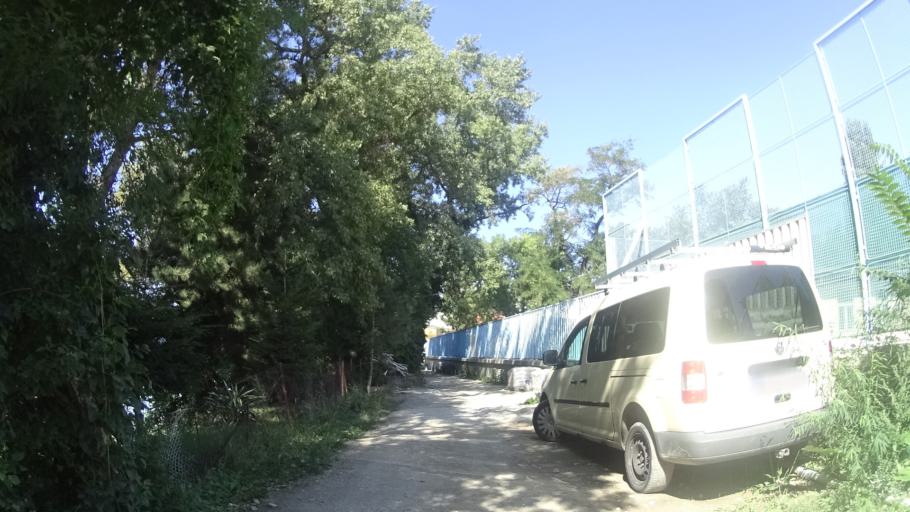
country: SK
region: Bratislavsky
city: Bratislava
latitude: 48.1446
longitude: 17.0722
